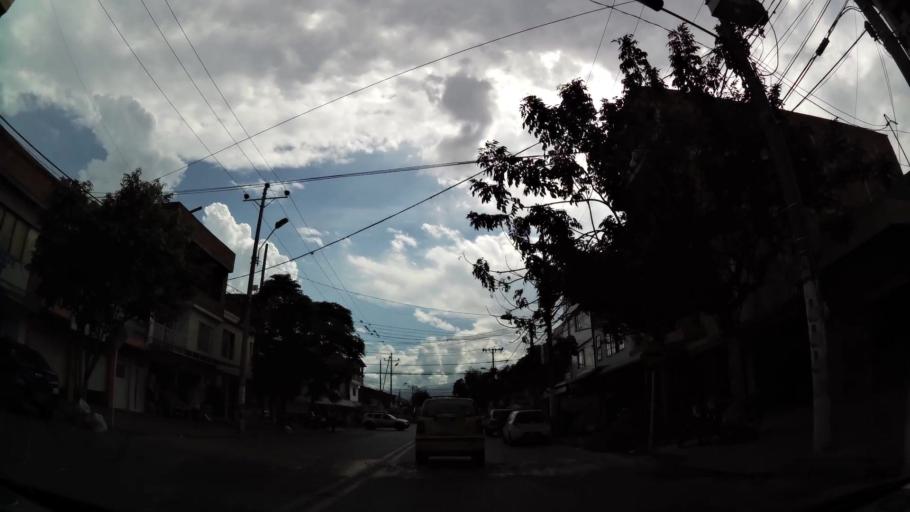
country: CO
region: Valle del Cauca
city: Cali
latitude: 3.4711
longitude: -76.5130
